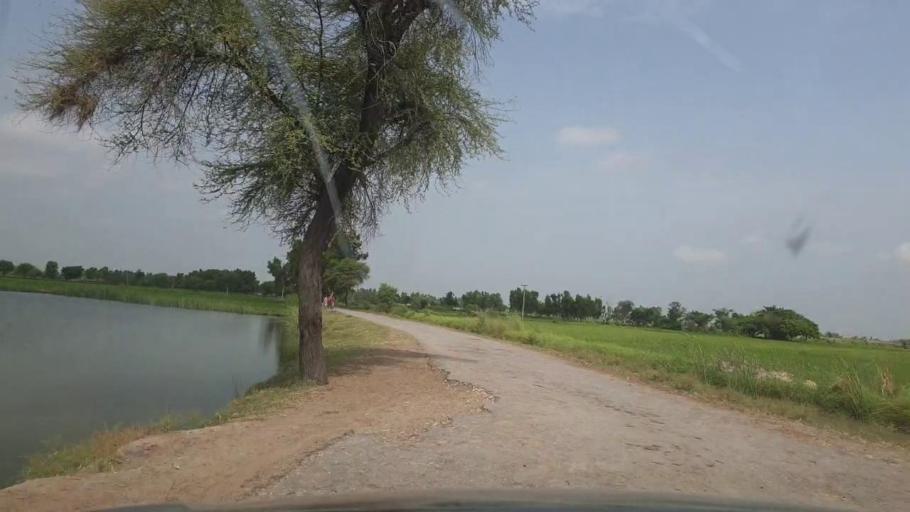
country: PK
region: Sindh
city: Ratodero
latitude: 27.8562
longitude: 68.2988
